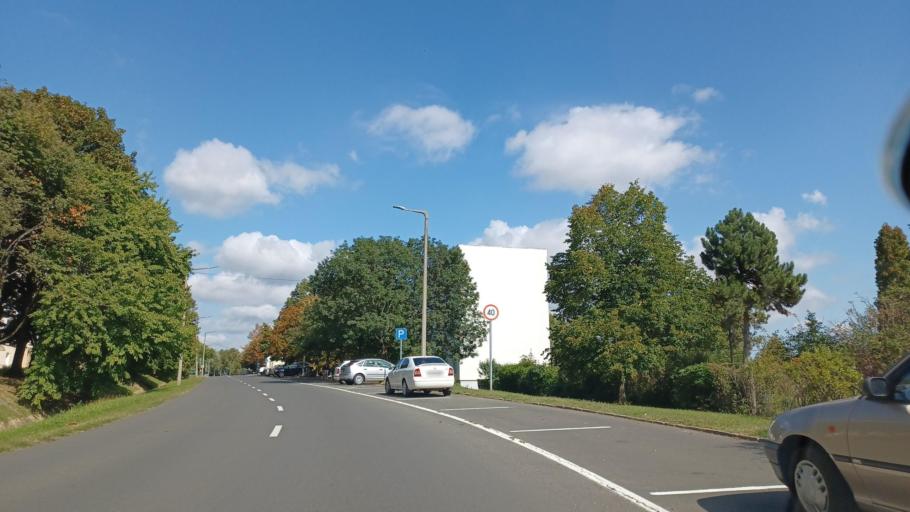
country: HU
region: Tolna
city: Szekszard
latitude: 46.3363
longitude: 18.6969
